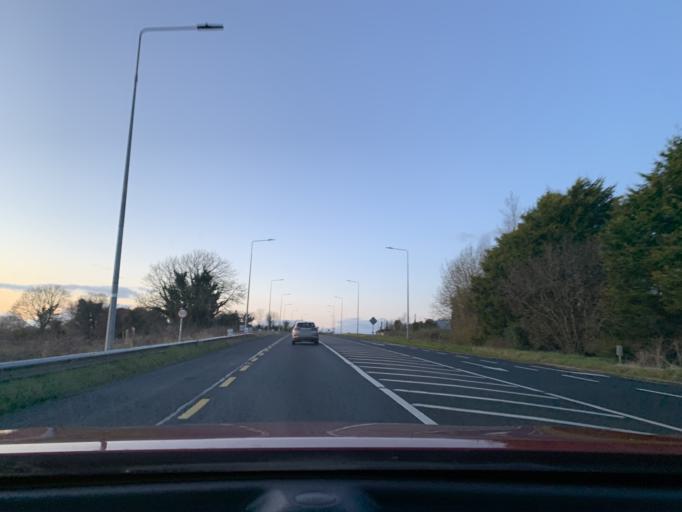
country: IE
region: Connaught
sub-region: County Leitrim
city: Carrick-on-Shannon
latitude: 53.8829
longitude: -7.9370
